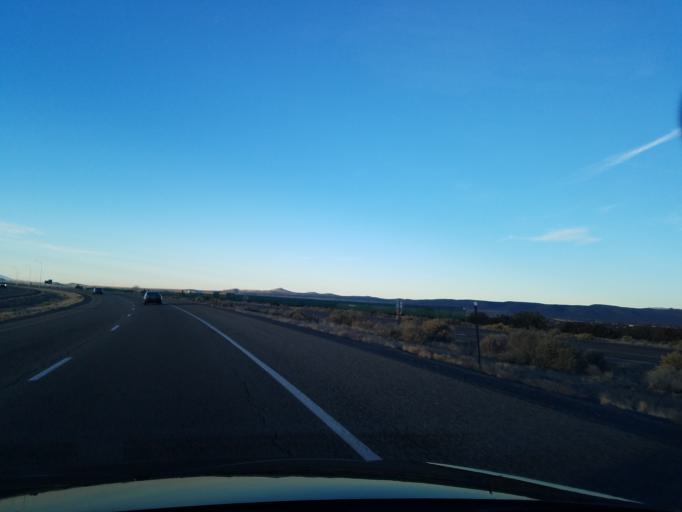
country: US
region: New Mexico
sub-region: Santa Fe County
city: Agua Fria
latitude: 35.6648
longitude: -106.0303
